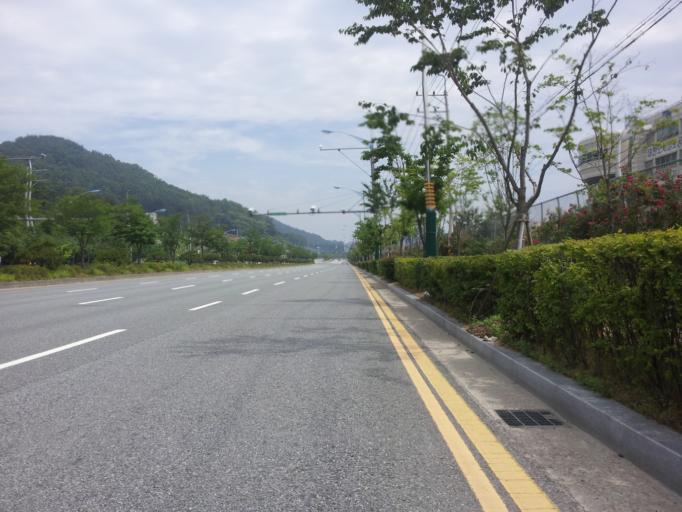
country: KR
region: Daejeon
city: Daejeon
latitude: 36.3228
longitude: 127.4724
